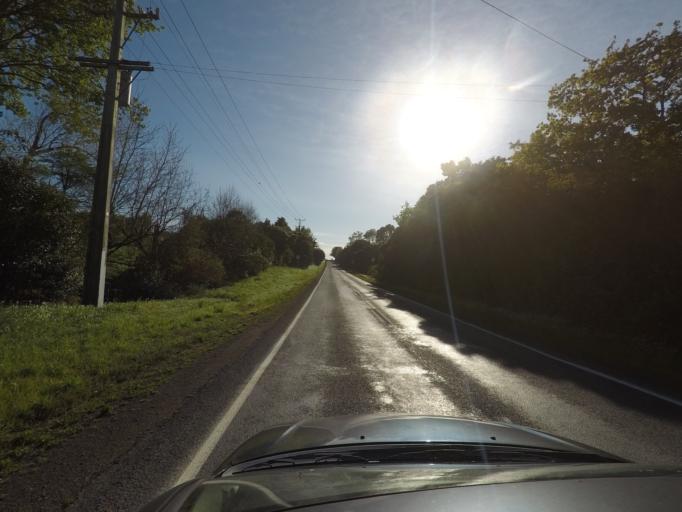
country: NZ
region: Auckland
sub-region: Auckland
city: Papakura
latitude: -37.0152
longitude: 174.9432
